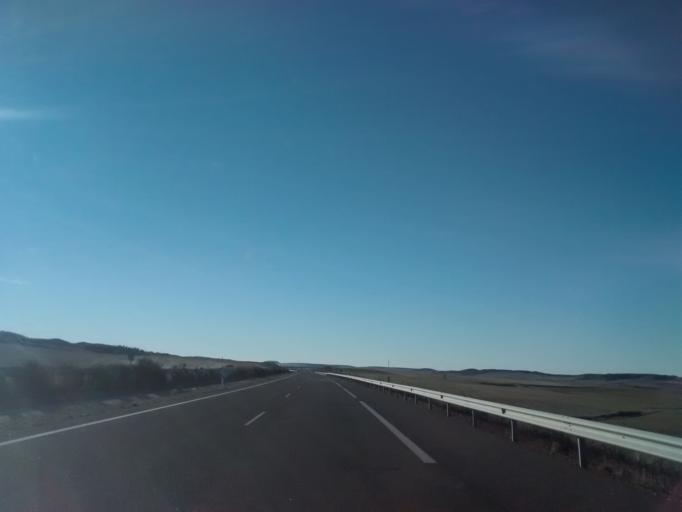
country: ES
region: Castille and Leon
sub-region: Provincia de Palencia
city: Pradanos de Ojeda
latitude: 42.6474
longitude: -4.3509
